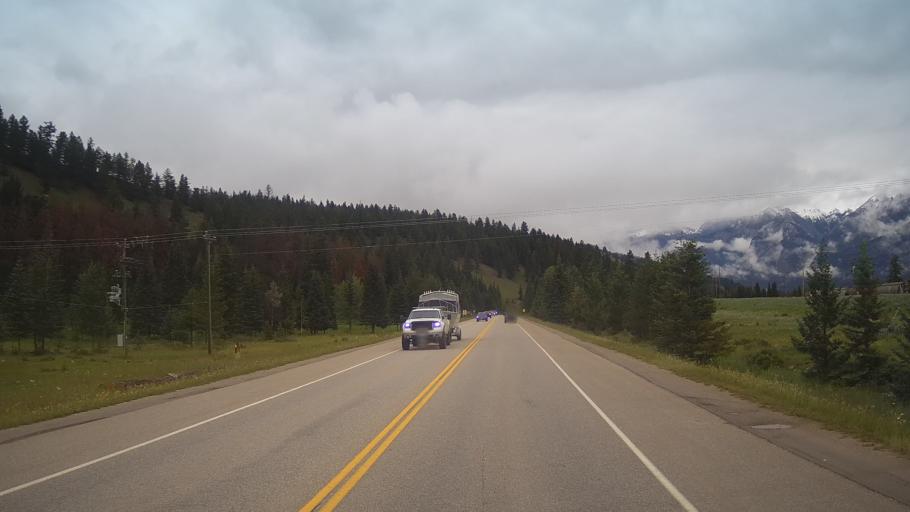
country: CA
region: Alberta
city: Jasper Park Lodge
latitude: 52.8901
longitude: -118.0763
